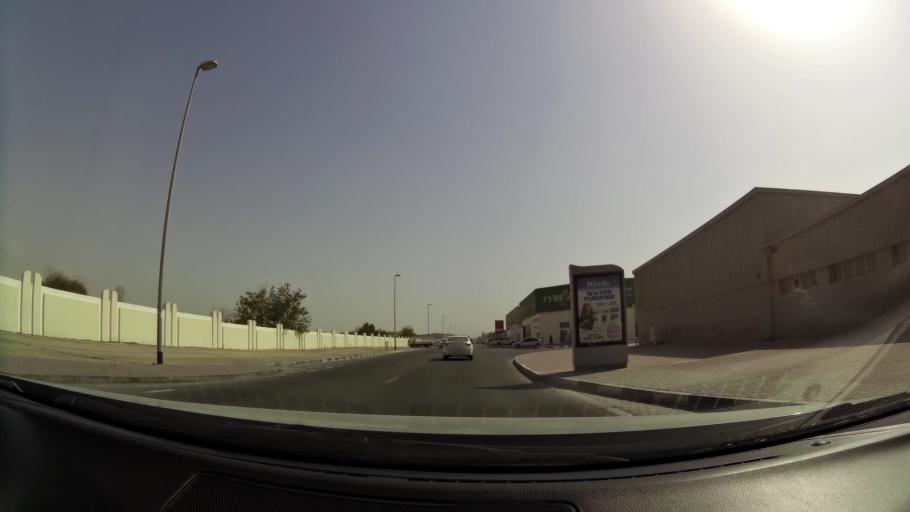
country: AE
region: Dubai
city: Dubai
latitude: 25.1672
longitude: 55.2408
